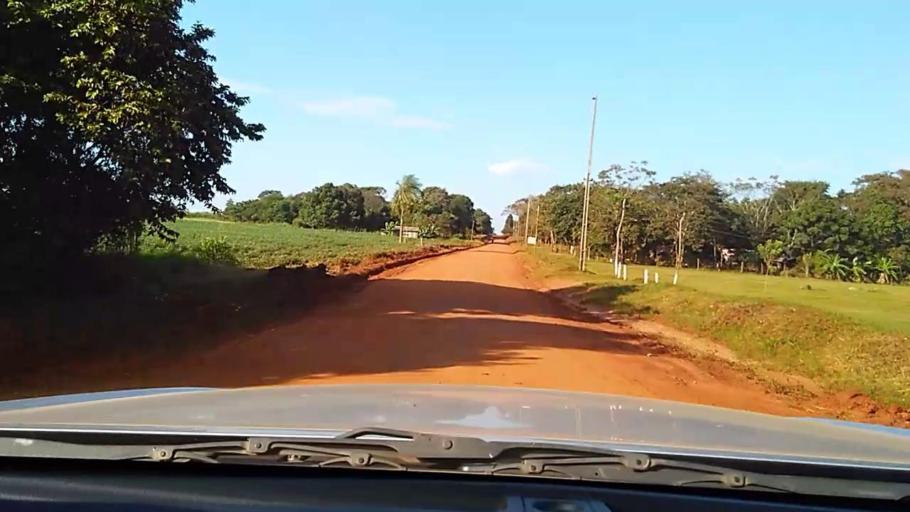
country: PY
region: Alto Parana
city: Doctor Juan Leon Mallorquin
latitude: -25.6866
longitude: -55.3767
